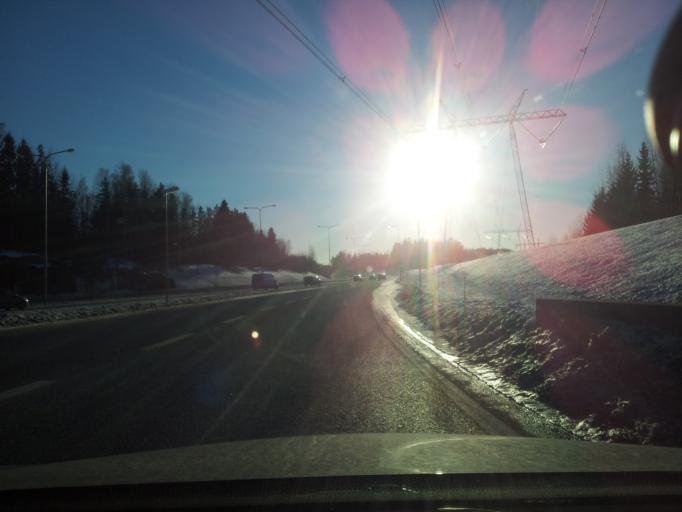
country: FI
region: Uusimaa
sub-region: Helsinki
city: Espoo
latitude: 60.2188
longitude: 24.6392
